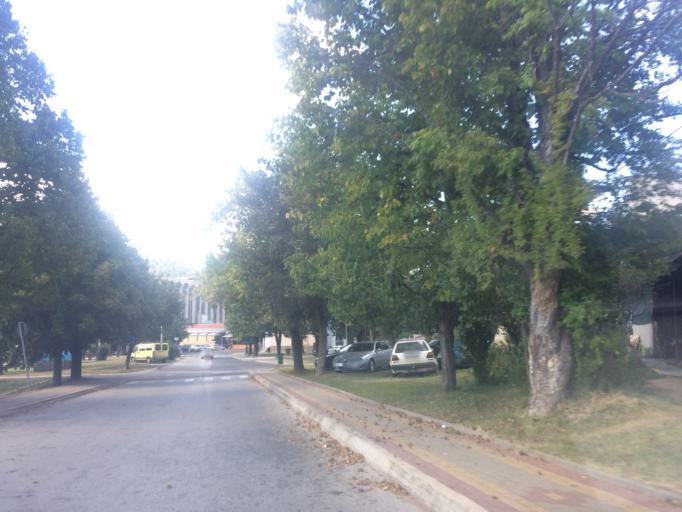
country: MK
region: Makedonska Kamenica
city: Makedonska Kamenica
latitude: 42.0206
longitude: 22.5907
